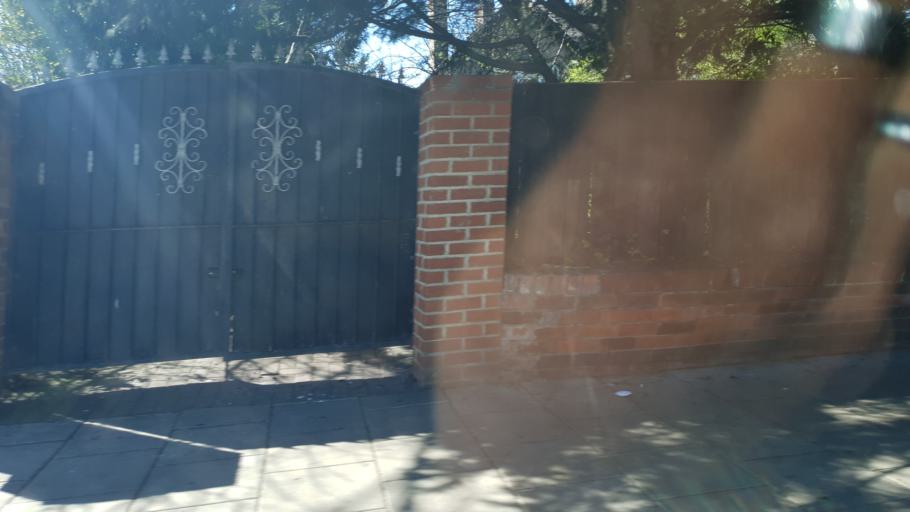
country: GB
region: England
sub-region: Middlesbrough
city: Middlesbrough
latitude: 54.5536
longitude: -1.2451
